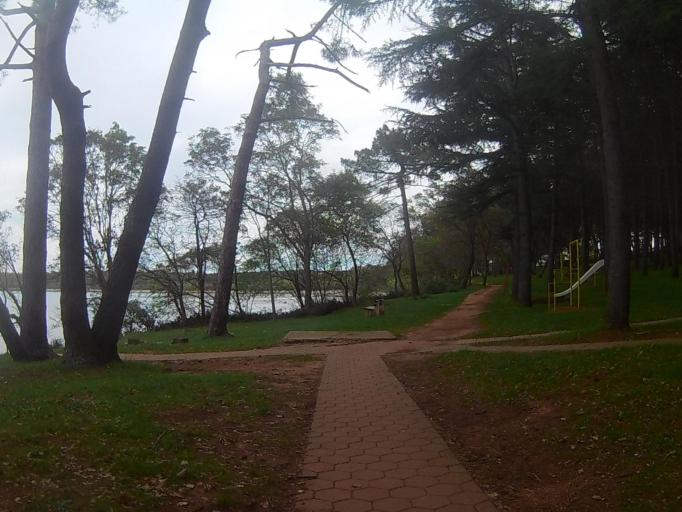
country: HR
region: Istarska
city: Novigrad
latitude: 45.3308
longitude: 13.5399
